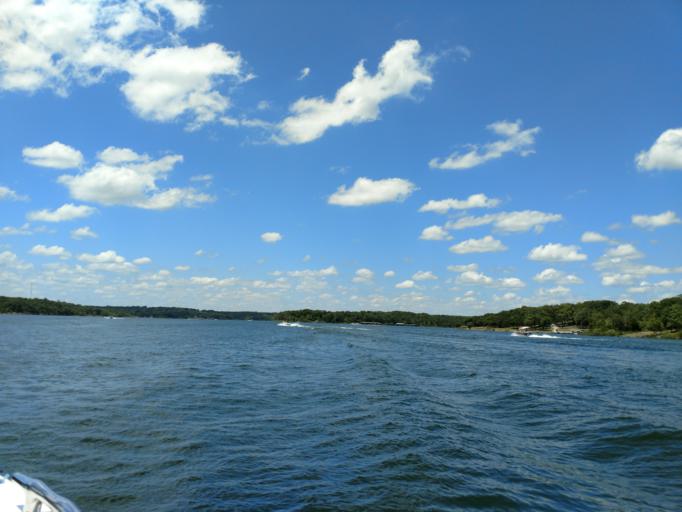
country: US
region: Missouri
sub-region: Barry County
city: Shell Knob
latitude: 36.5895
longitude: -93.5568
